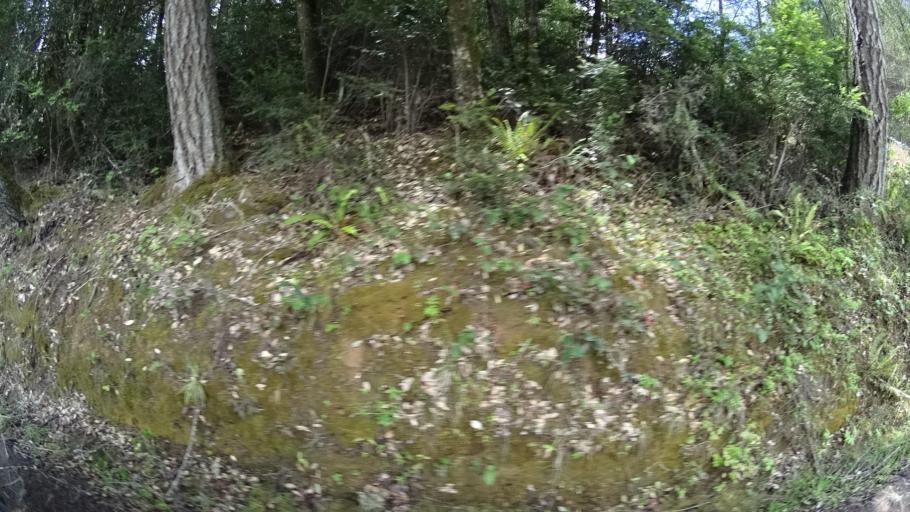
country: US
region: California
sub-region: Humboldt County
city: Blue Lake
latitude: 40.8005
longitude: -123.8770
